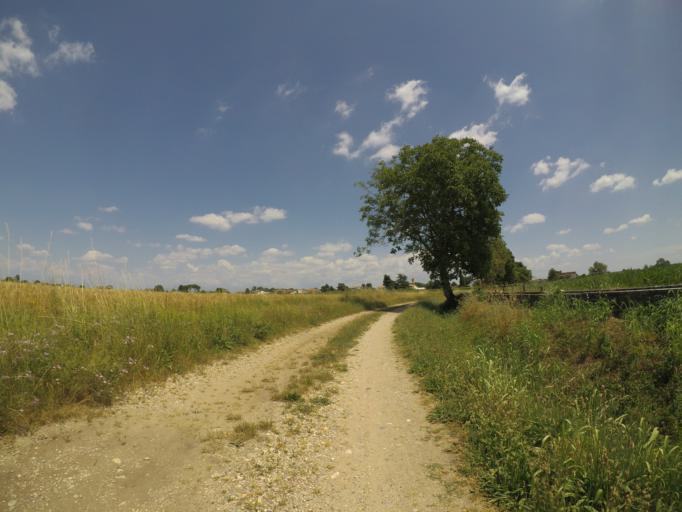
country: IT
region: Friuli Venezia Giulia
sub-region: Provincia di Udine
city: Bertiolo
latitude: 45.9365
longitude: 13.0644
